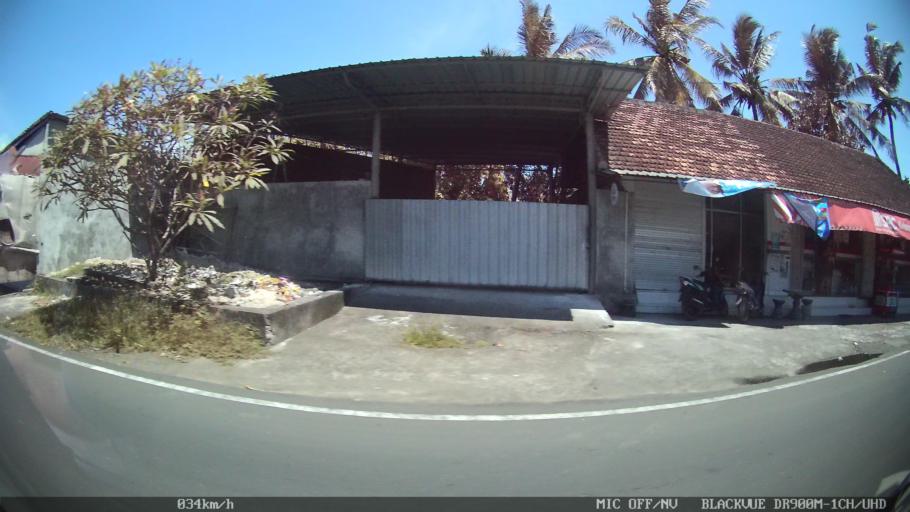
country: ID
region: Bali
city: Banjar Pasekan
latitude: -8.5715
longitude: 115.3290
